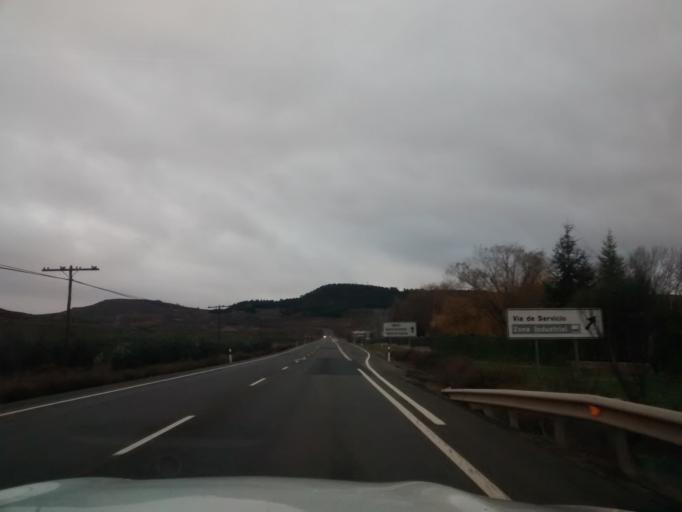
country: ES
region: La Rioja
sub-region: Provincia de La Rioja
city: Fuenmayor
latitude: 42.4649
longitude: -2.6018
